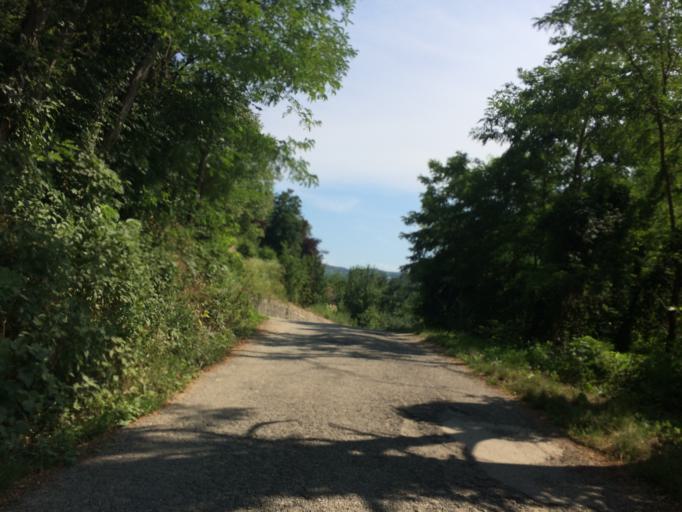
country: IT
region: Piedmont
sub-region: Provincia di Cuneo
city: Cortemilia
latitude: 44.5719
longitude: 8.2023
